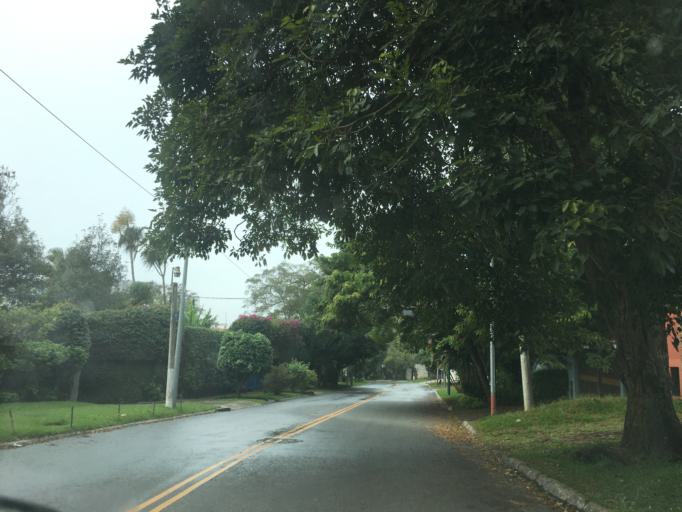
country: GT
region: Guatemala
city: Santa Catarina Pinula
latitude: 14.5816
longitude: -90.4876
